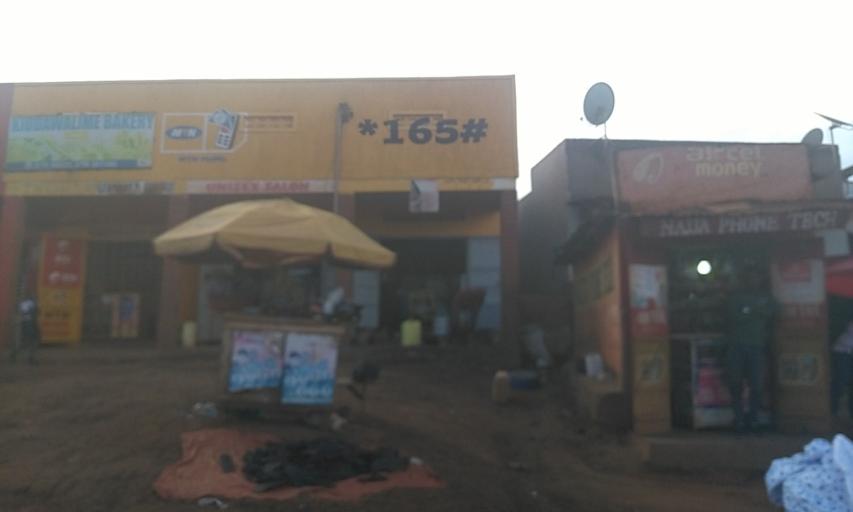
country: UG
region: Central Region
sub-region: Wakiso District
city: Kajansi
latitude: 0.2552
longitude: 32.5066
